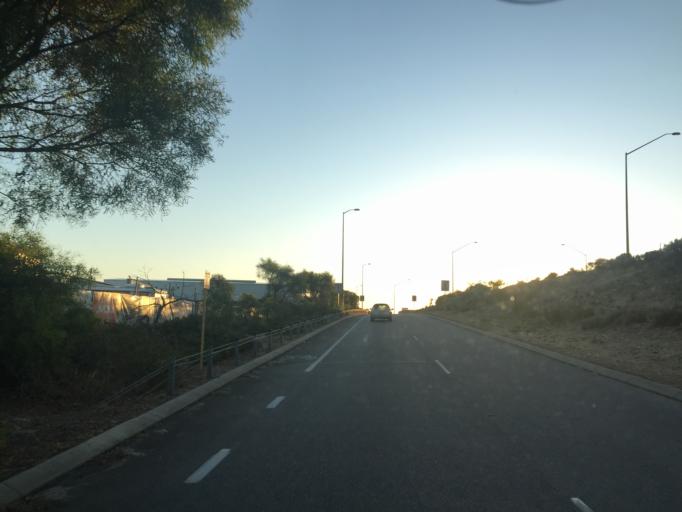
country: AU
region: Western Australia
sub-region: Belmont
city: Kewdale
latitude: -31.9861
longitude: 115.9347
